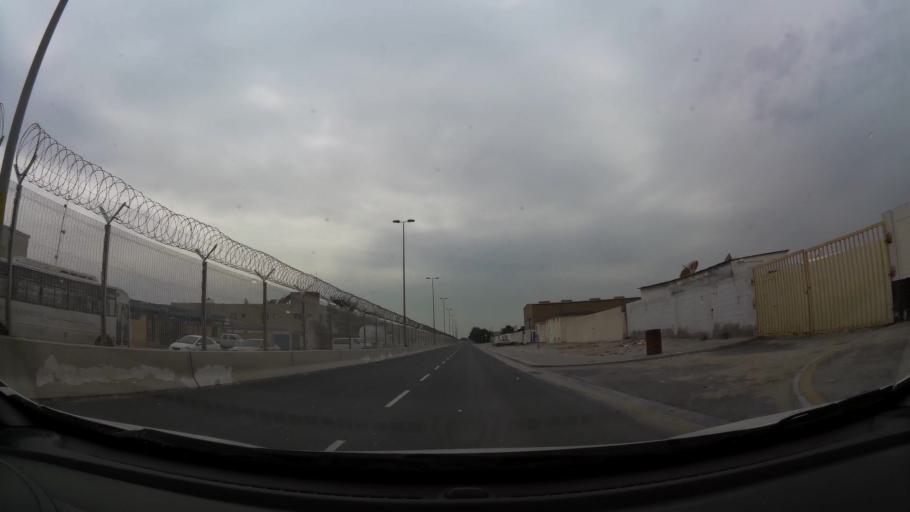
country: BH
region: Northern
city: Sitrah
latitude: 26.1807
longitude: 50.6065
